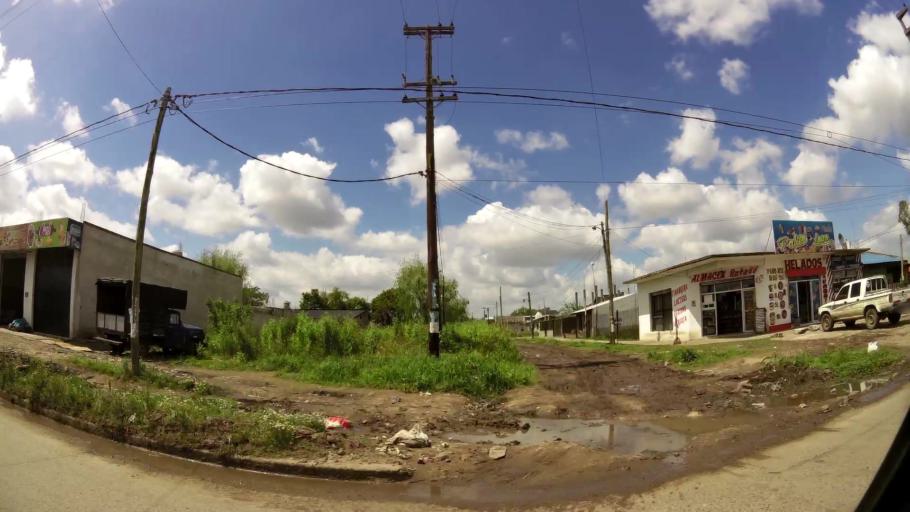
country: AR
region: Buenos Aires
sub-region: Partido de Quilmes
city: Quilmes
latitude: -34.8321
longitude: -58.2319
